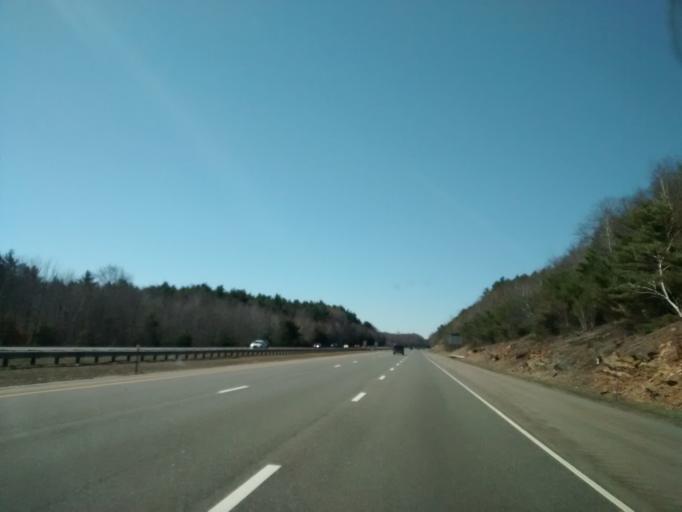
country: US
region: Massachusetts
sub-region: Hampden County
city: Holland
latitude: 42.0038
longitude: -72.1636
